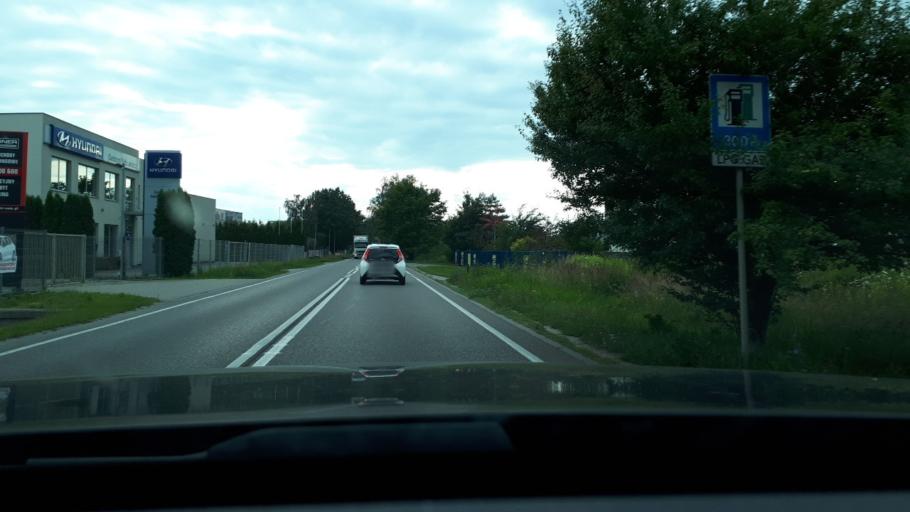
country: PL
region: Masovian Voivodeship
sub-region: Powiat pruszkowski
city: Michalowice
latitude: 52.1446
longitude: 20.8571
